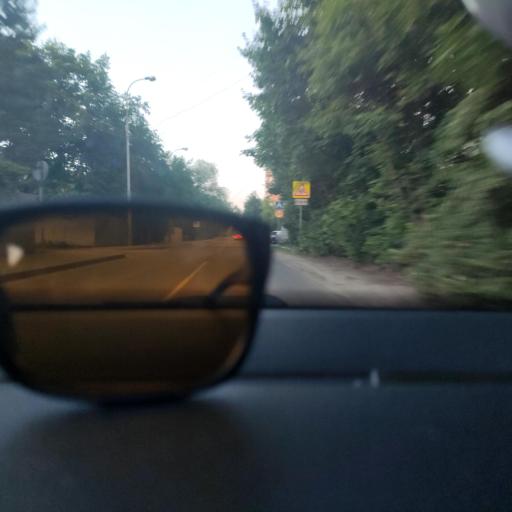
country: RU
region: Moskovskaya
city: Troitsk
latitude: 55.4881
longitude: 37.3059
